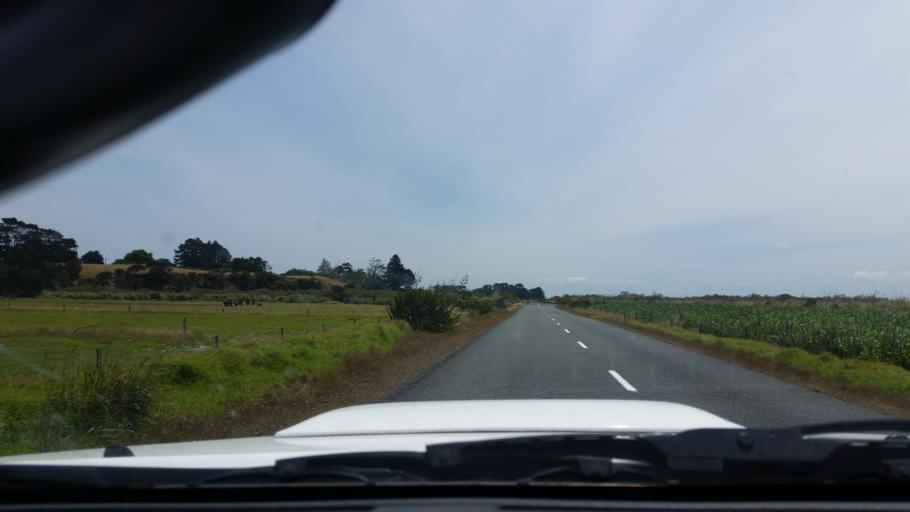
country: NZ
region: Northland
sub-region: Kaipara District
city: Dargaville
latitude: -36.1784
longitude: 174.0292
